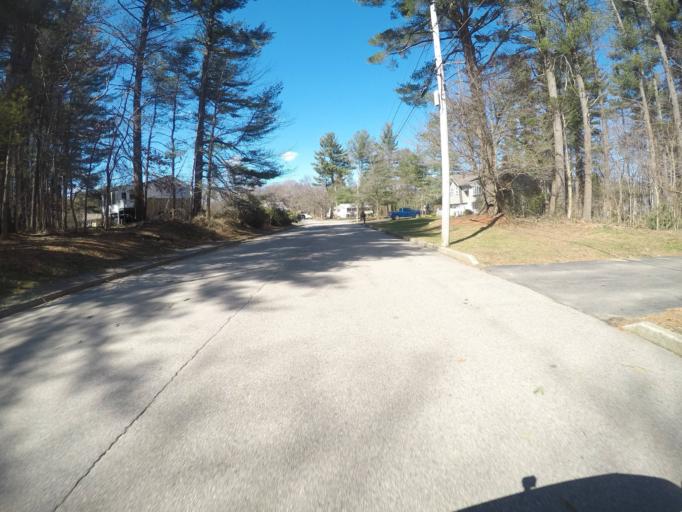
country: US
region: Massachusetts
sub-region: Bristol County
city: Easton
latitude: 42.0074
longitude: -71.1020
